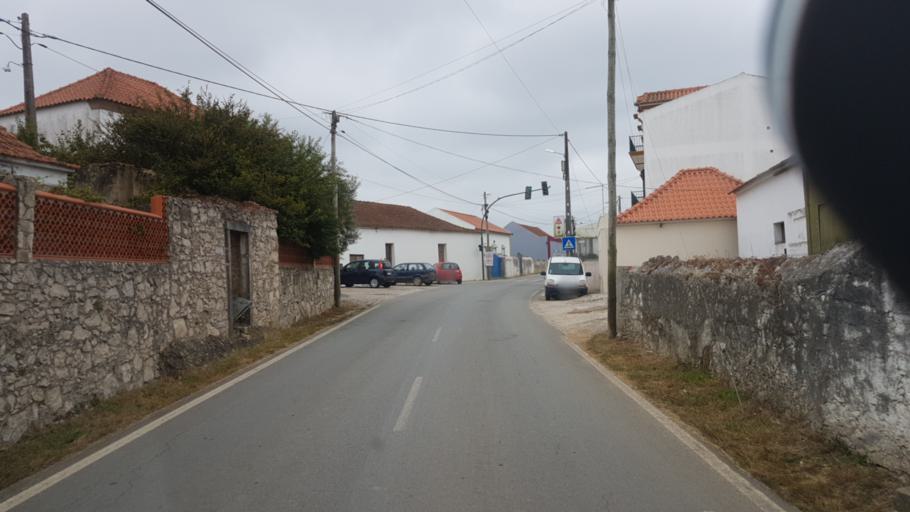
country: PT
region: Leiria
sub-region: Bombarral
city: Bombarral
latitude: 39.2813
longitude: -9.1903
